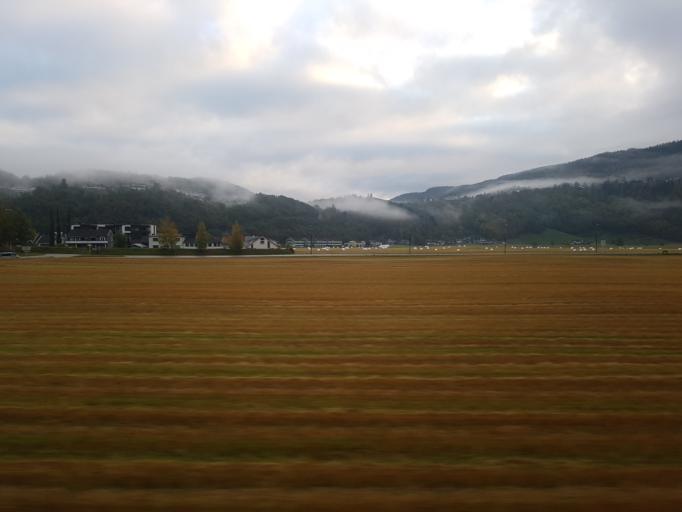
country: NO
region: Sor-Trondelag
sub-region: Melhus
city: Melhus
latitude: 63.2844
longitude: 10.2846
